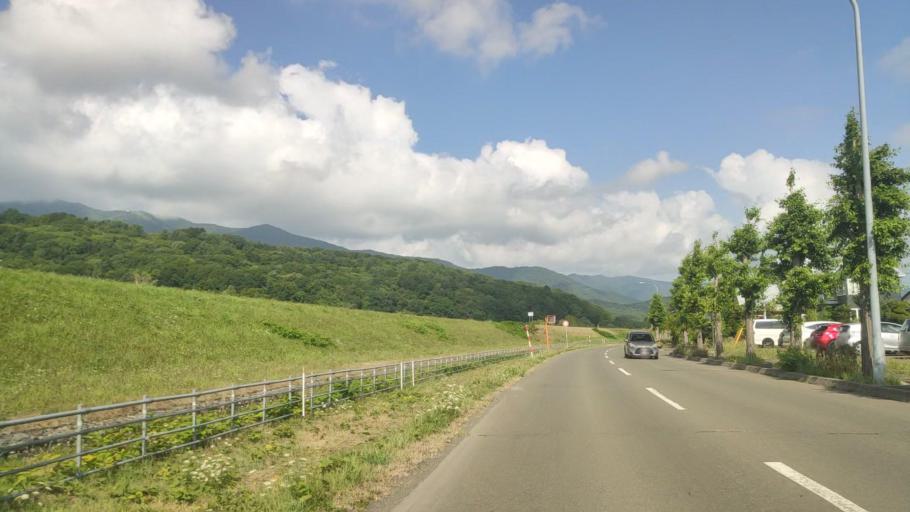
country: JP
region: Hokkaido
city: Shimo-furano
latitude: 43.3399
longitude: 142.3812
